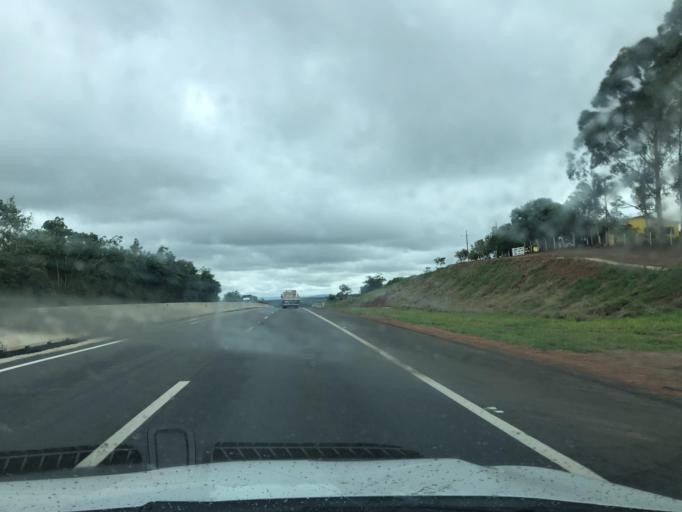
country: BR
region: Goias
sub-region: Catalao
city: Catalao
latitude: -18.2595
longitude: -47.9990
